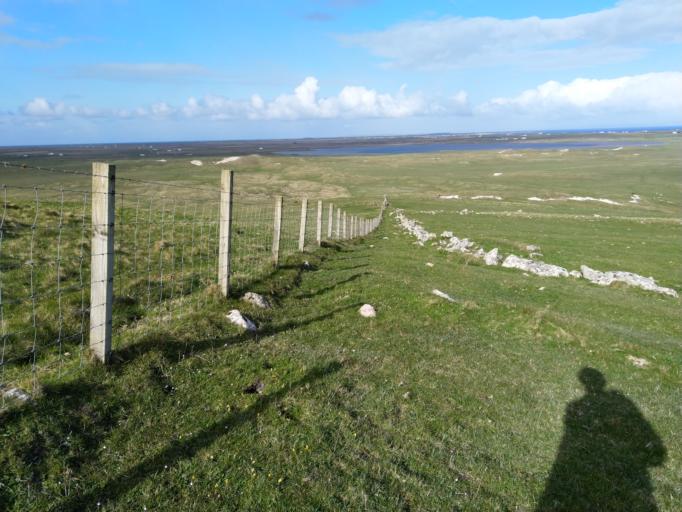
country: GB
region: Scotland
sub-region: Eilean Siar
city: Barra
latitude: 56.4620
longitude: -6.9687
